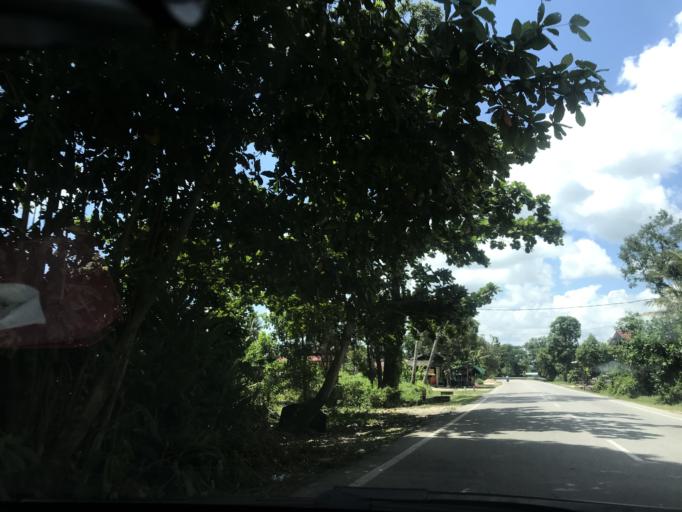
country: MY
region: Kelantan
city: Tumpat
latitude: 6.1980
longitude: 102.1310
